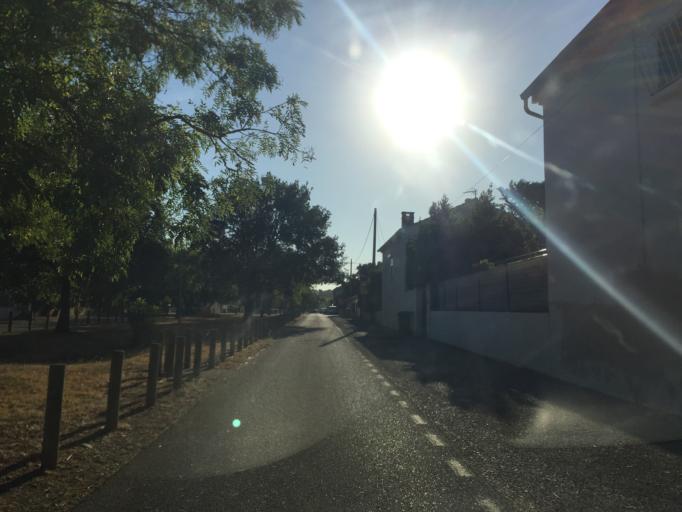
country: FR
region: Provence-Alpes-Cote d'Azur
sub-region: Departement du Vaucluse
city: Sorgues
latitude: 44.0094
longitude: 4.8815
